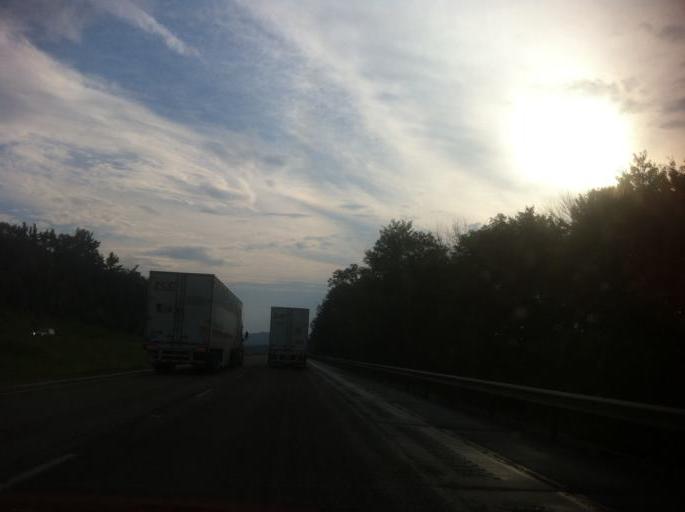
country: US
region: Pennsylvania
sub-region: Clarion County
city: Knox
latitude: 41.1827
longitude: -79.6794
